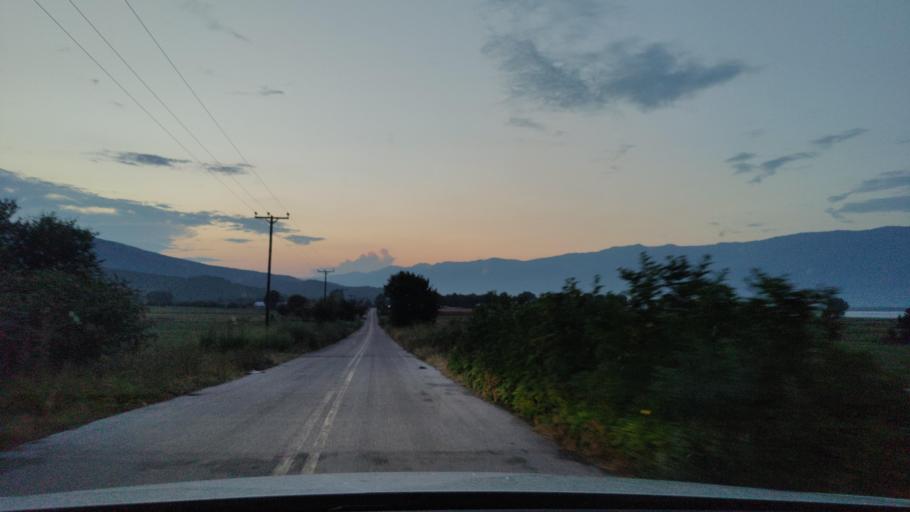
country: GR
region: Central Macedonia
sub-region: Nomos Serron
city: Chrysochorafa
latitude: 41.1777
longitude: 23.1135
